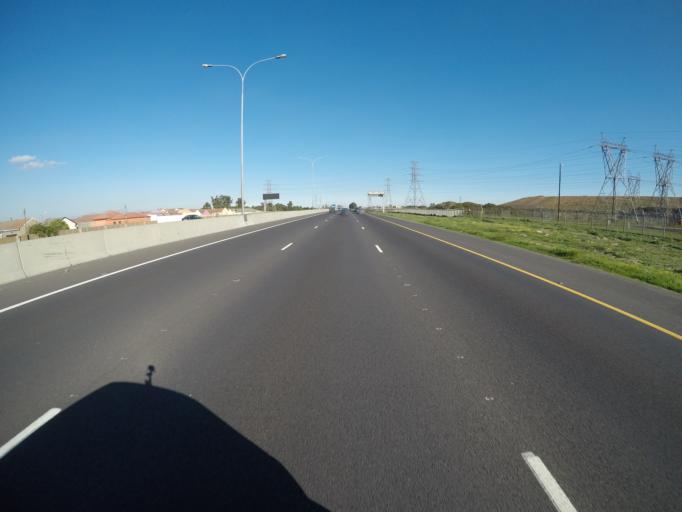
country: ZA
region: Western Cape
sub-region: City of Cape Town
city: Kraaifontein
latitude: -33.9344
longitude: 18.6614
